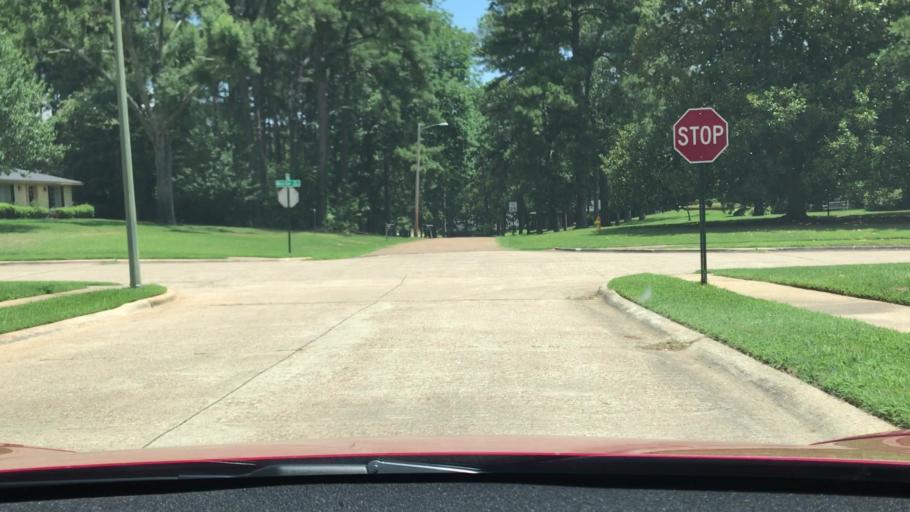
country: US
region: Louisiana
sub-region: Bossier Parish
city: Bossier City
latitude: 32.4324
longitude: -93.7337
